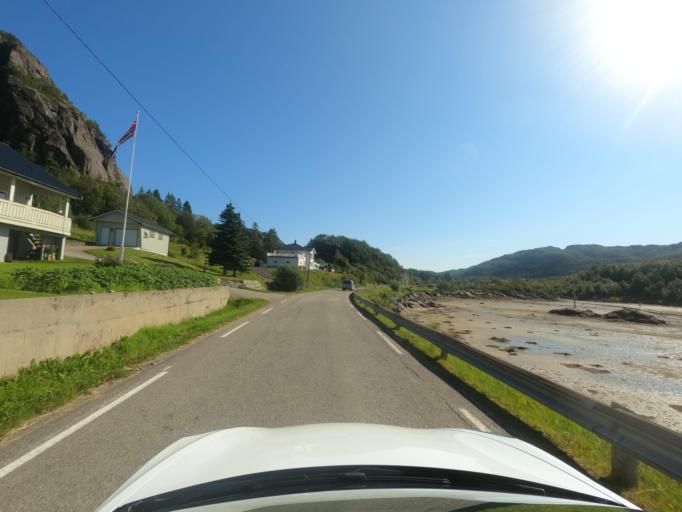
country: NO
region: Nordland
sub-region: Hadsel
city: Stokmarknes
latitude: 68.3046
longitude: 15.0054
